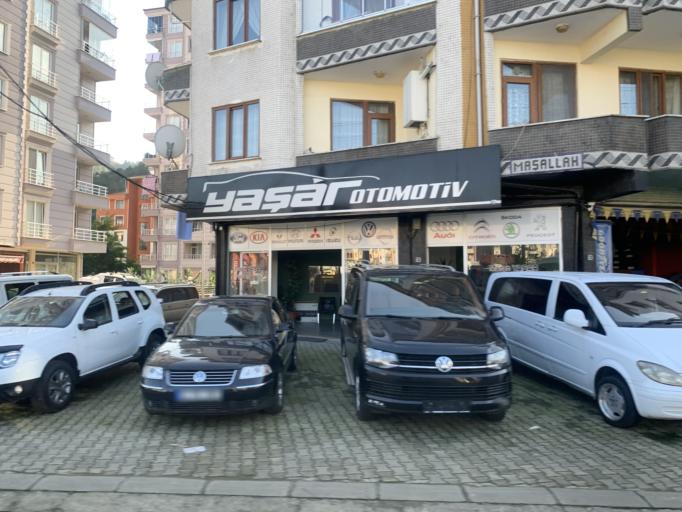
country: TR
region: Trabzon
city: Of
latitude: 40.9425
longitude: 40.2667
